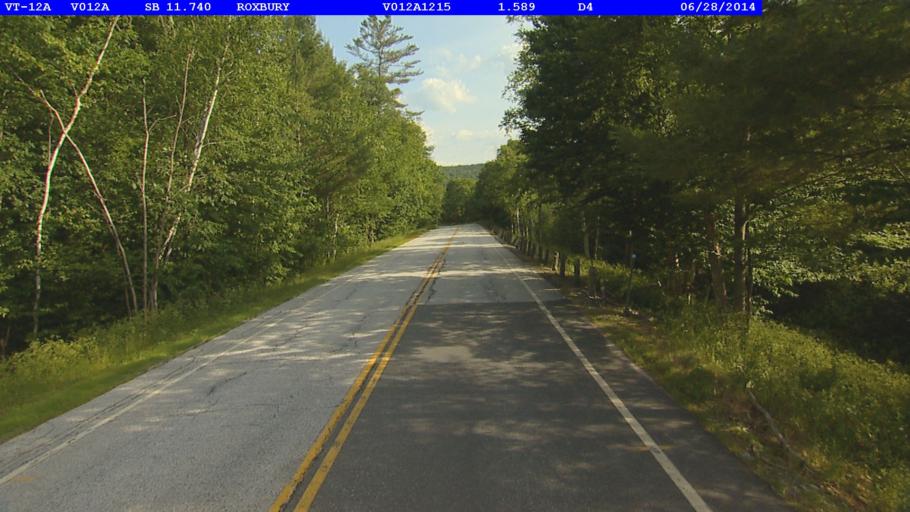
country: US
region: Vermont
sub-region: Washington County
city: Northfield
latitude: 44.0514
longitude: -72.7438
